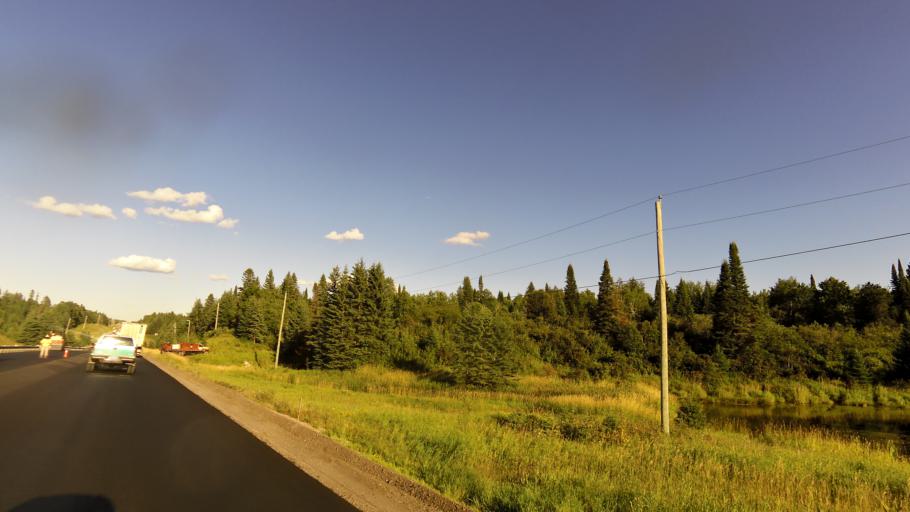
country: CA
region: Ontario
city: Dryden
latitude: 49.8151
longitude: -92.8787
